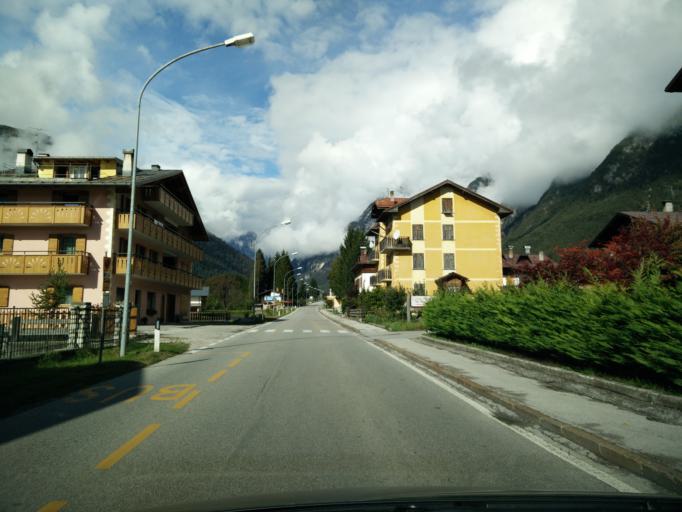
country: IT
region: Veneto
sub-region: Provincia di Belluno
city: Auronzo
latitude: 46.5634
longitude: 12.4128
